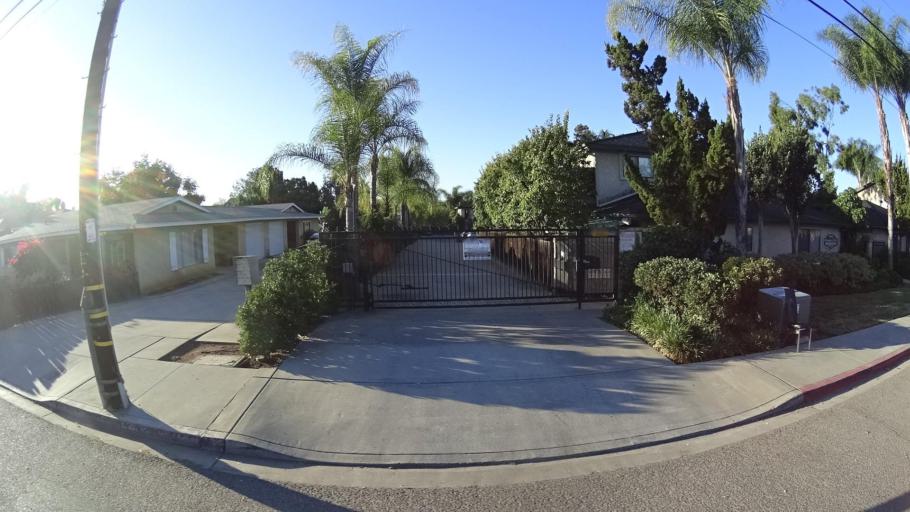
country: US
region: California
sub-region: San Diego County
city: Bostonia
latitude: 32.8115
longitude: -116.9425
